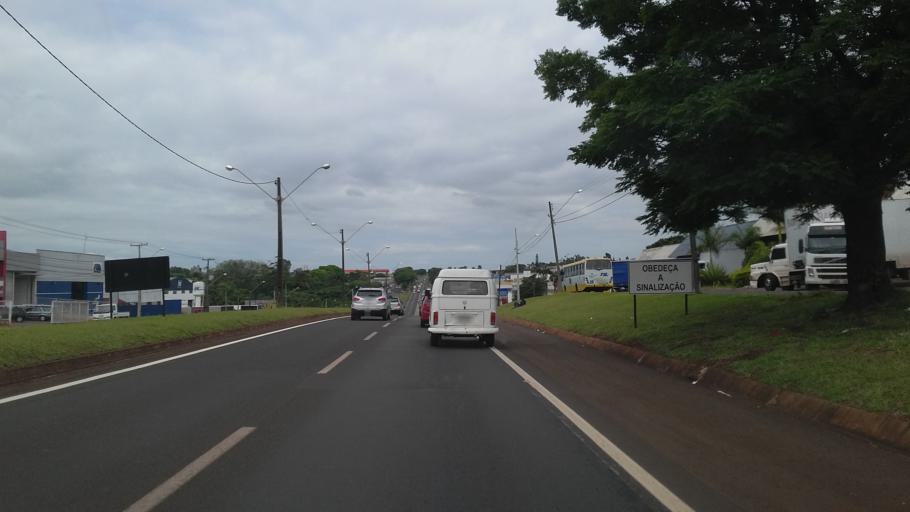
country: BR
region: Parana
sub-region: Londrina
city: Londrina
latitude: -23.2931
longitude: -51.1282
